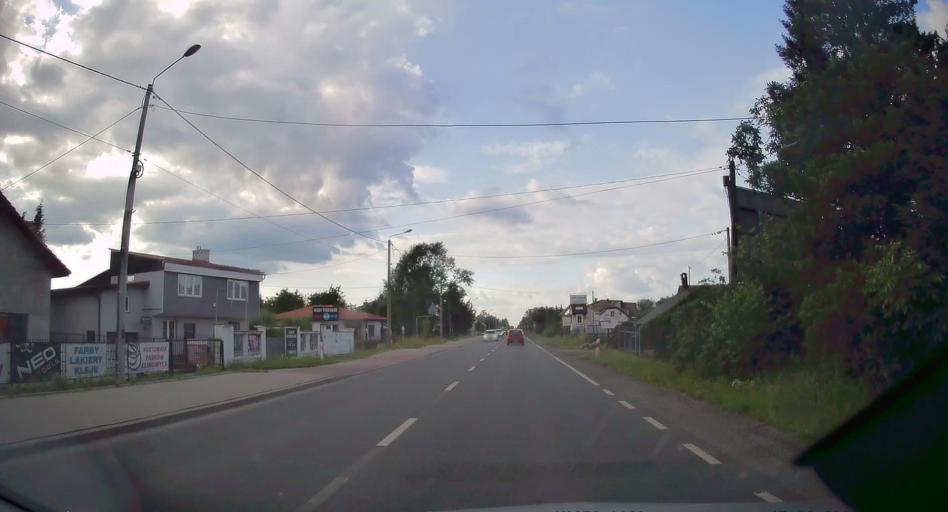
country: PL
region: Lesser Poland Voivodeship
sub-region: Powiat oswiecimski
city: Kety
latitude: 49.8938
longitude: 19.2188
